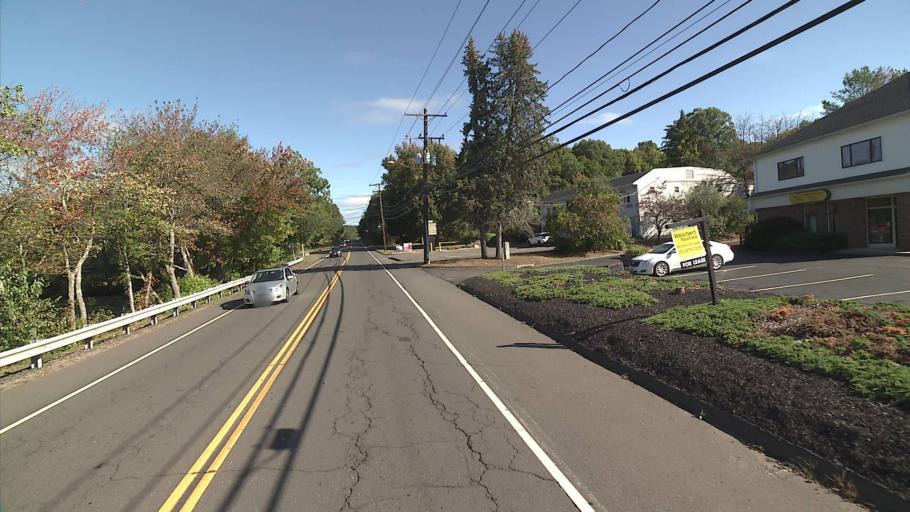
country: US
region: Connecticut
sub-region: New Haven County
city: Wolcott
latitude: 41.5828
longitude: -72.9942
